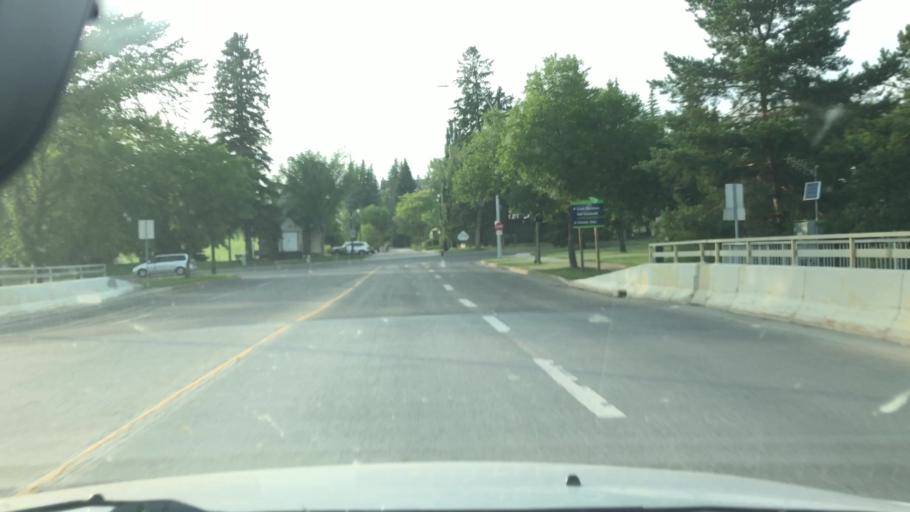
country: CA
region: Alberta
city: St. Albert
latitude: 53.6356
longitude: -113.6272
